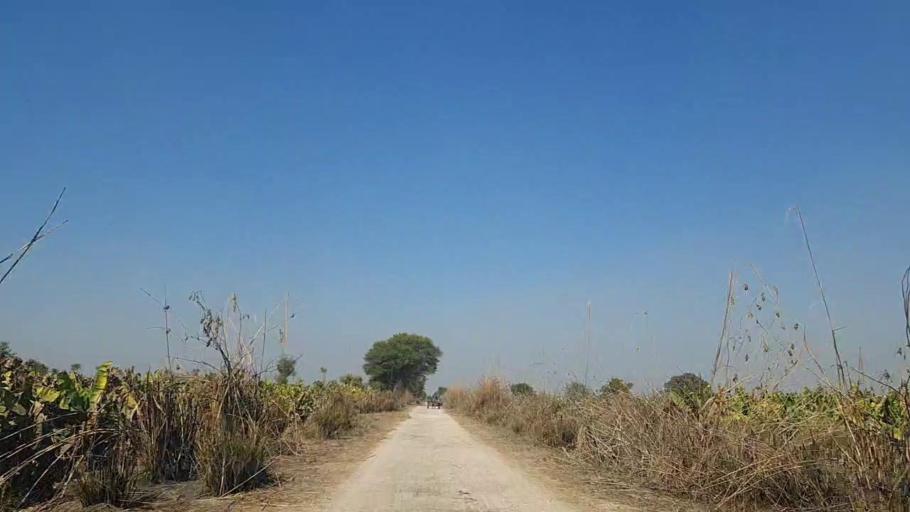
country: PK
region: Sindh
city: Sakrand
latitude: 26.2610
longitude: 68.2209
